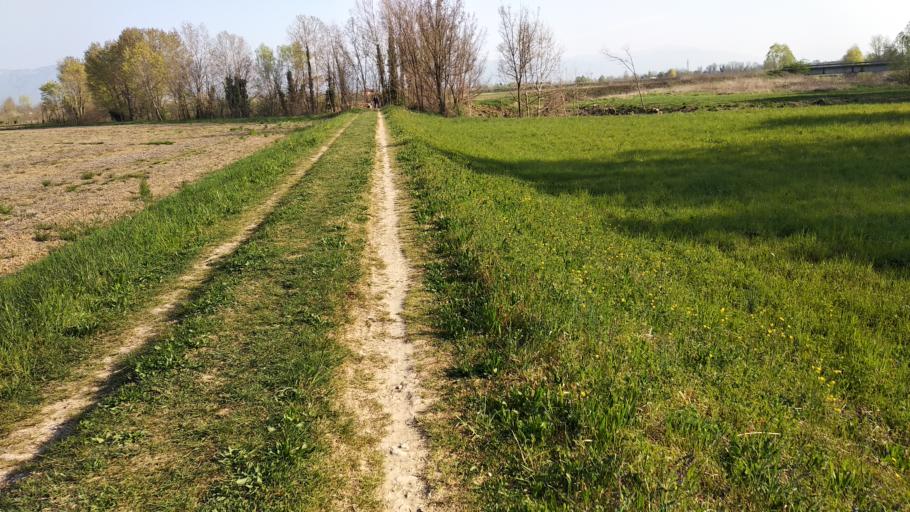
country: IT
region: Veneto
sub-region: Provincia di Vicenza
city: Crispi Cavour
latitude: 45.5868
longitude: 11.5353
